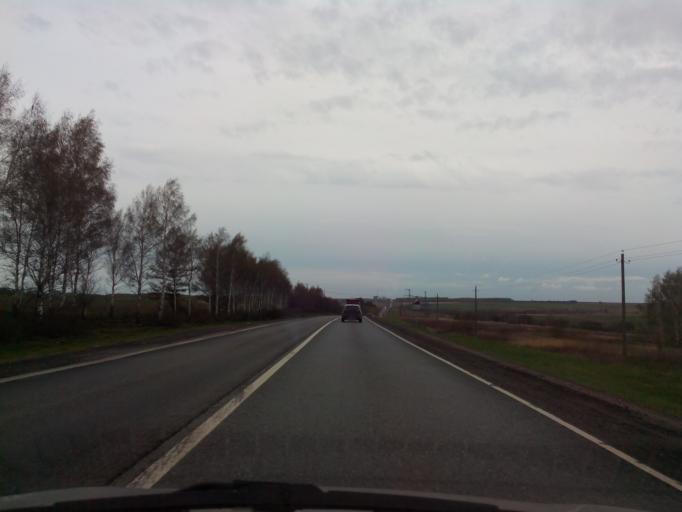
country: RU
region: Moskovskaya
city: Ozherel'ye
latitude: 54.7340
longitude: 38.2587
